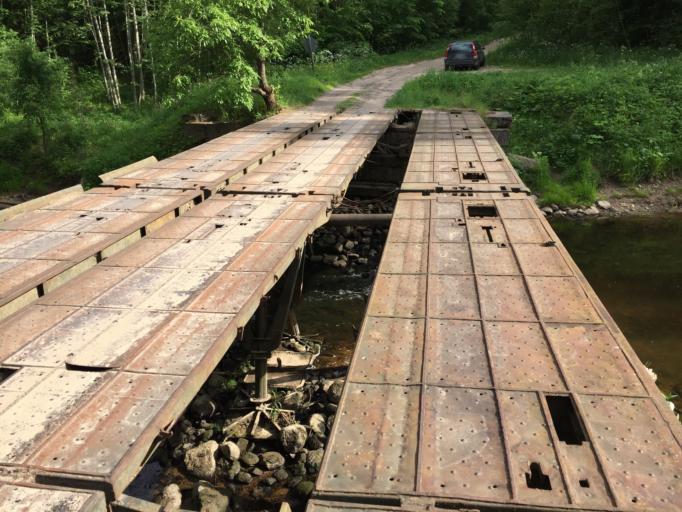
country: LV
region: Dobeles Rajons
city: Dobele
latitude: 56.6603
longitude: 23.1825
